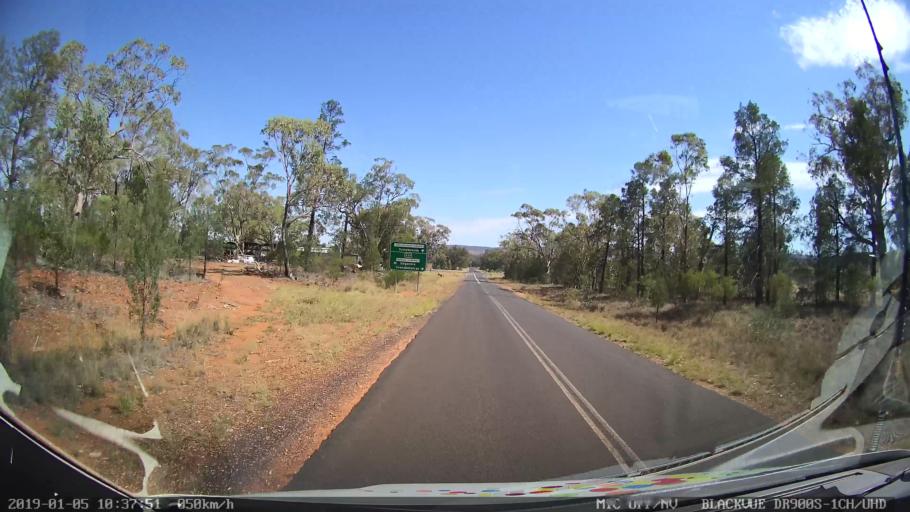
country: AU
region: New South Wales
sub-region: Gilgandra
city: Gilgandra
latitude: -31.4717
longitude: 148.9206
